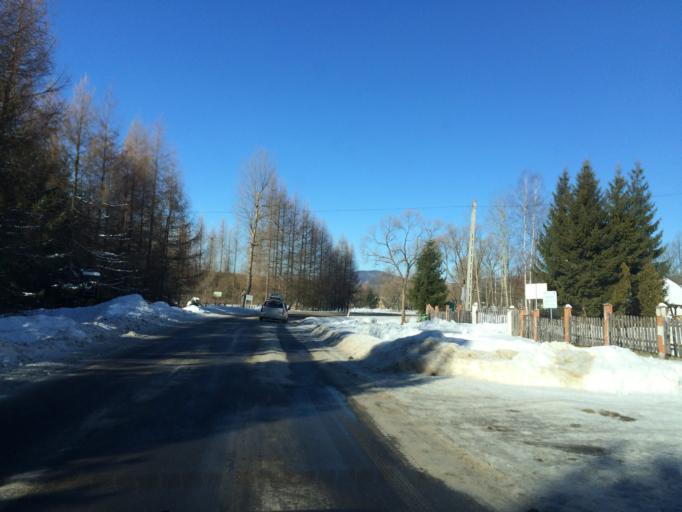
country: PL
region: Subcarpathian Voivodeship
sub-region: Powiat leski
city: Cisna
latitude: 49.1554
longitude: 22.4687
